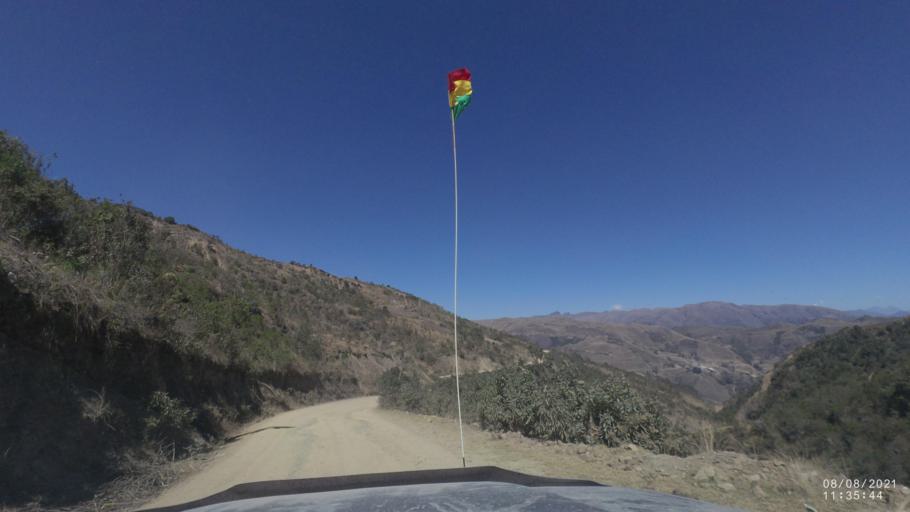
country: BO
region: Cochabamba
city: Colchani
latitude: -16.7780
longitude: -66.6442
